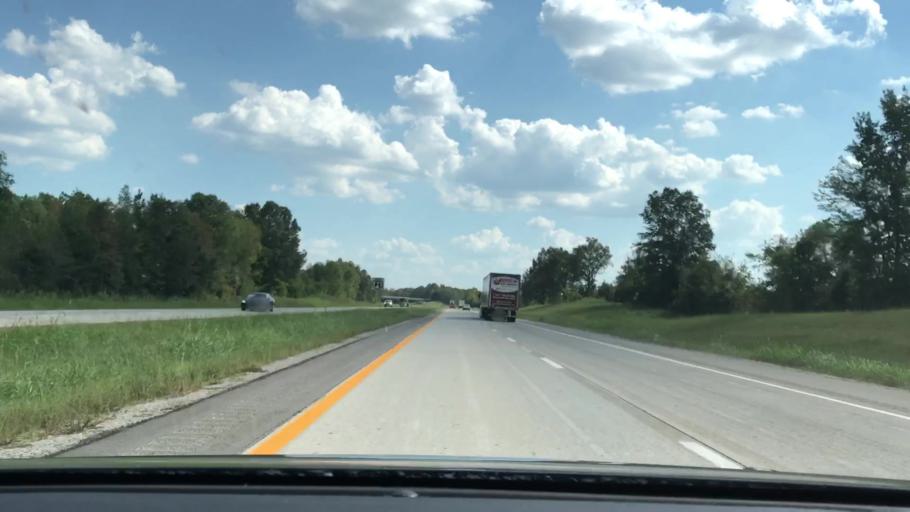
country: US
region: Kentucky
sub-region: Ohio County
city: Oak Grove
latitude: 37.3572
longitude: -86.7906
